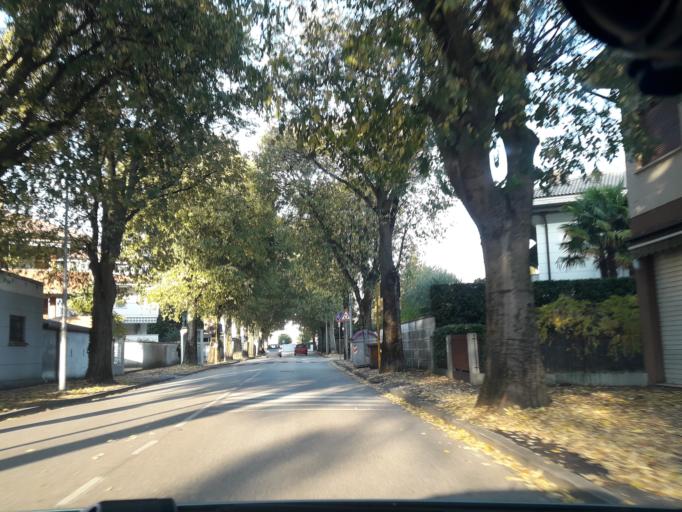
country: IT
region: Friuli Venezia Giulia
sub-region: Provincia di Udine
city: Udine
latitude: 46.0819
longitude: 13.2405
